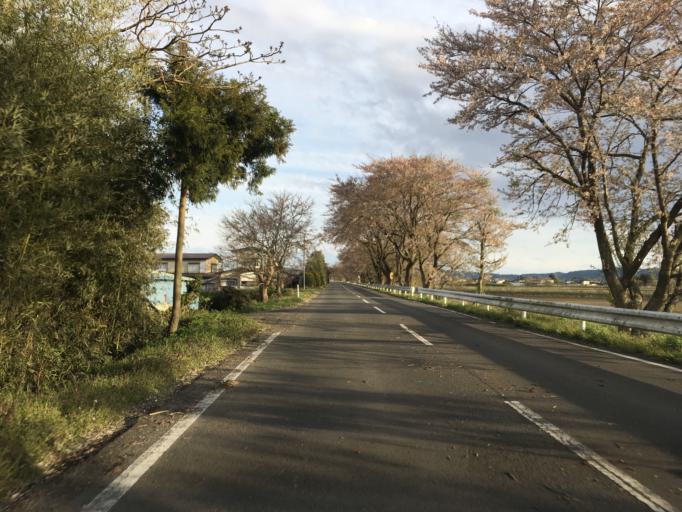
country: JP
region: Miyagi
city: Wakuya
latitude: 38.6496
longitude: 141.1443
